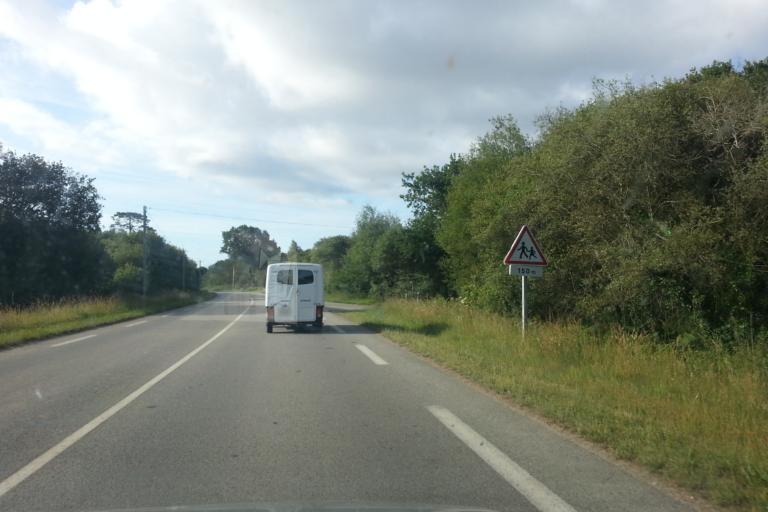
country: FR
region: Brittany
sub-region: Departement du Morbihan
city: Merlevenez
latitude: 47.7196
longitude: -3.2295
